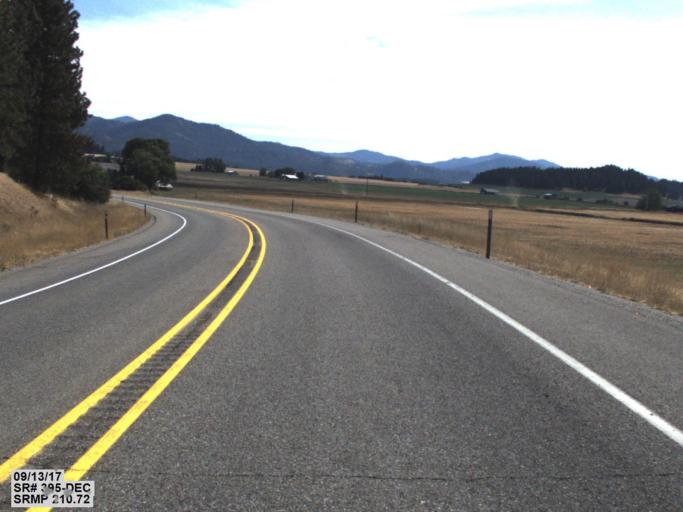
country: US
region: Washington
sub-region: Stevens County
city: Chewelah
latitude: 48.3037
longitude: -117.7750
